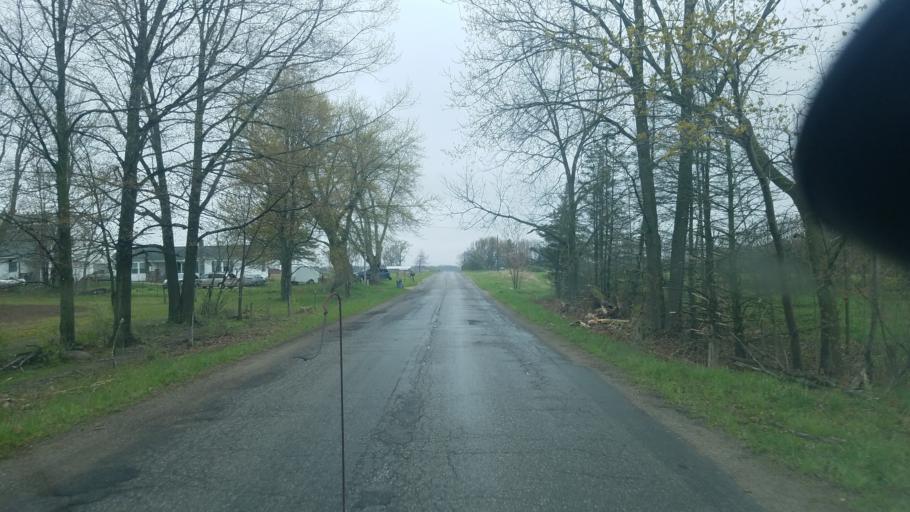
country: US
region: Michigan
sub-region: Mecosta County
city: Canadian Lakes
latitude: 43.5647
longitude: -85.3441
